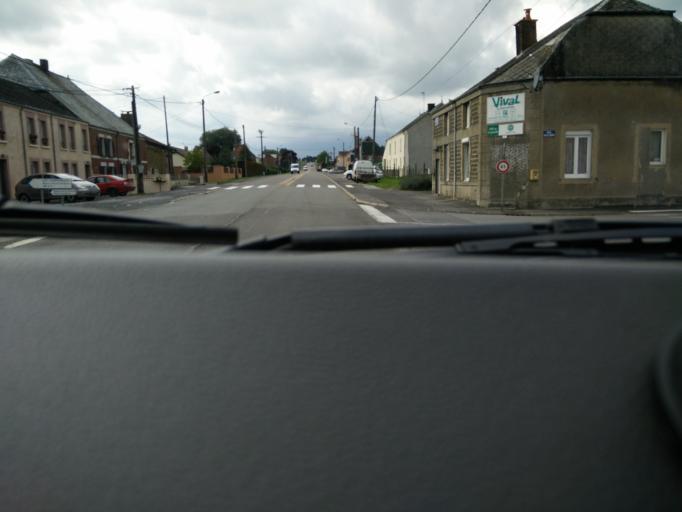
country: FR
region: Champagne-Ardenne
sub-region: Departement des Ardennes
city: Signy-le-Petit
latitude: 49.8723
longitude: 4.3834
